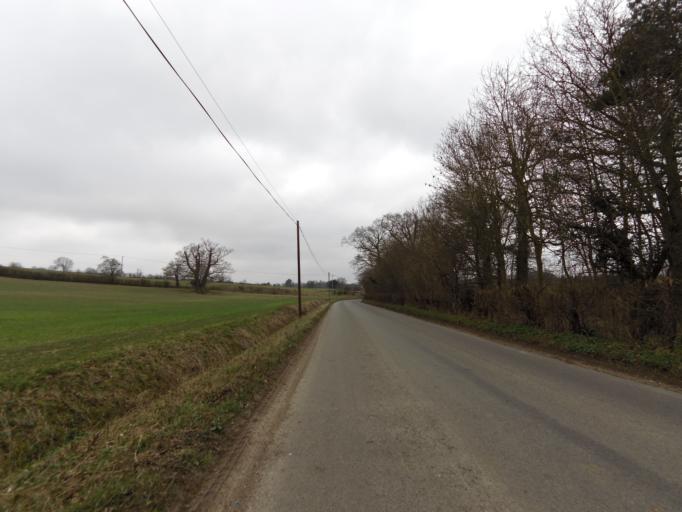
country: GB
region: England
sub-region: Suffolk
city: Cookley
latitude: 52.2813
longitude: 1.4591
